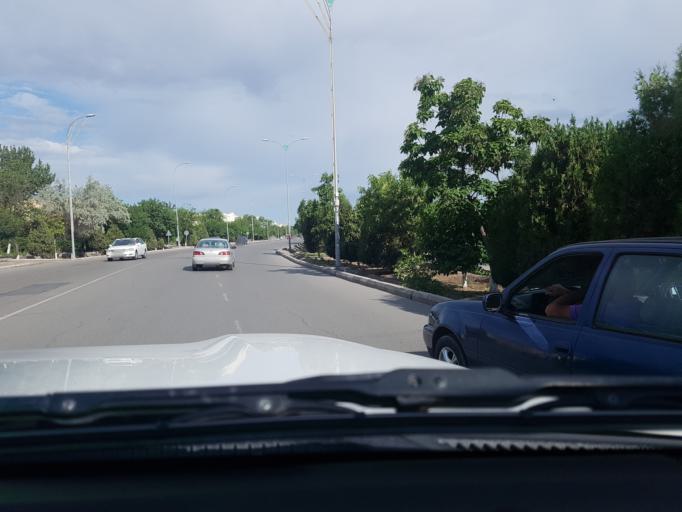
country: TM
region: Dasoguz
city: Dasoguz
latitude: 41.8410
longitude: 59.9416
